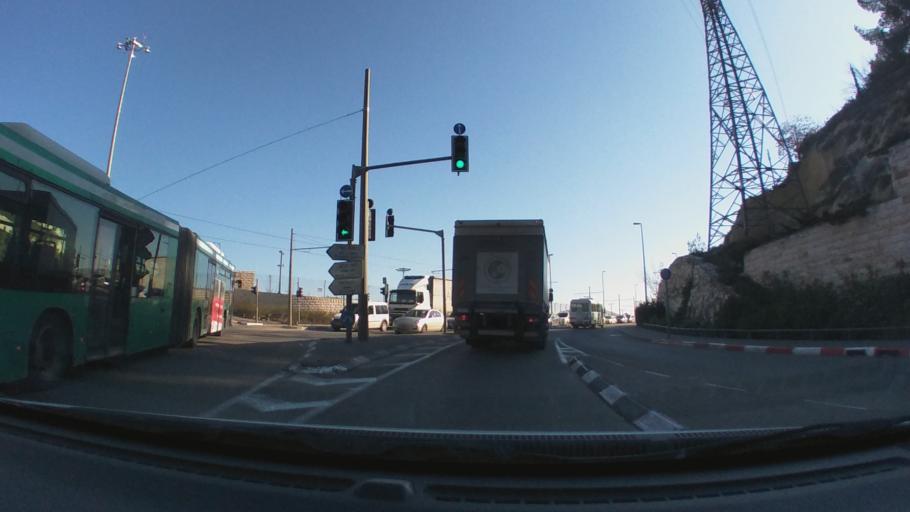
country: PS
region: West Bank
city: `Anata
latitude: 31.8082
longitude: 35.2355
